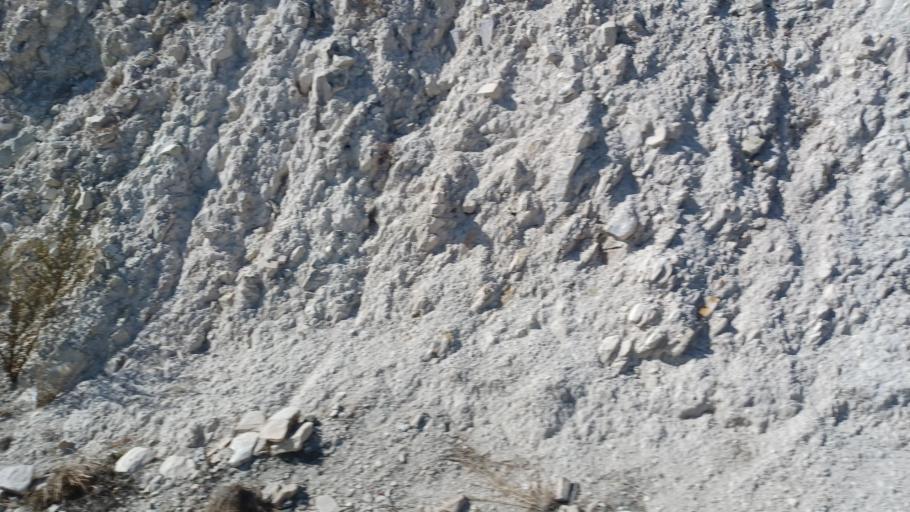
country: CY
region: Limassol
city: Pyrgos
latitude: 34.7614
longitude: 33.2291
